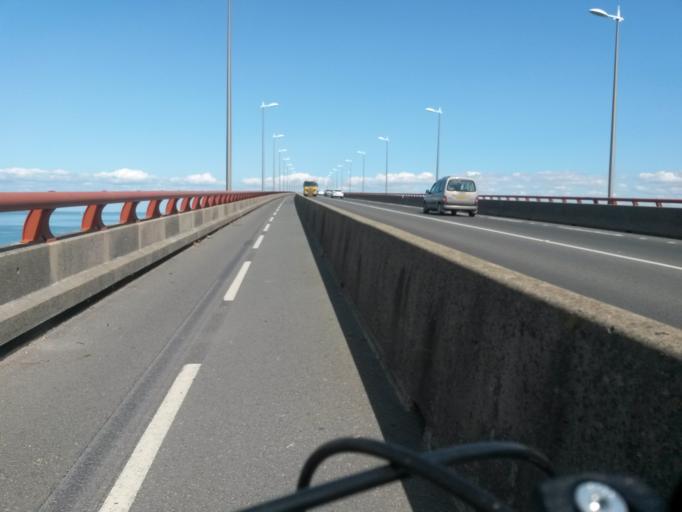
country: FR
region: Poitou-Charentes
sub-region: Departement de la Charente-Maritime
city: Rivedoux-Plage
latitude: 46.1658
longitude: -1.2531
